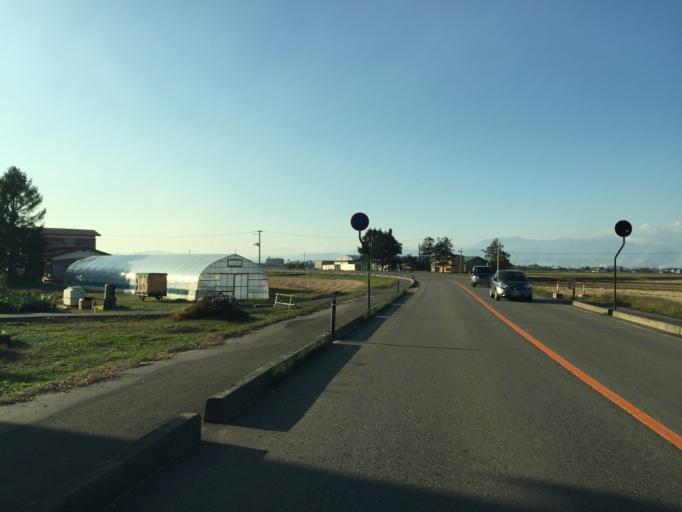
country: JP
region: Fukushima
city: Kitakata
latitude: 37.5548
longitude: 139.9037
